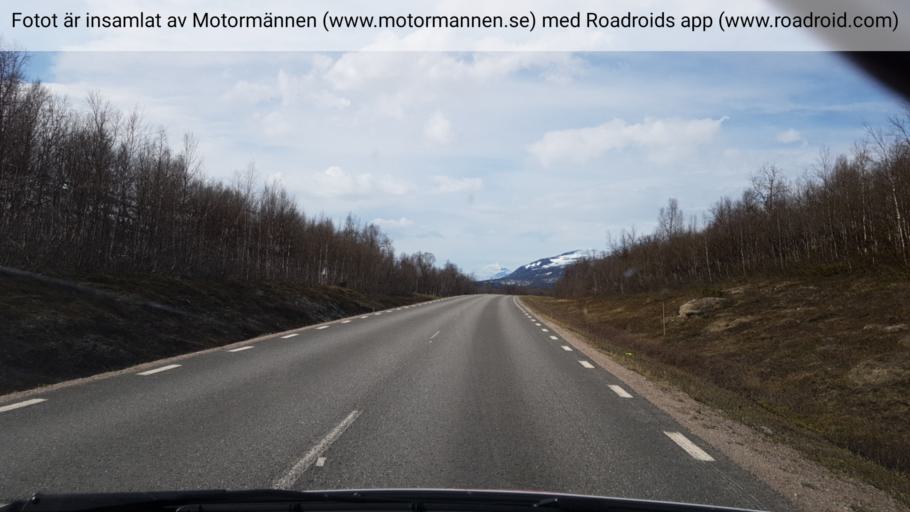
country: NO
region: Nordland
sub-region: Sorfold
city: Straumen
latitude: 66.6296
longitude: 16.2114
